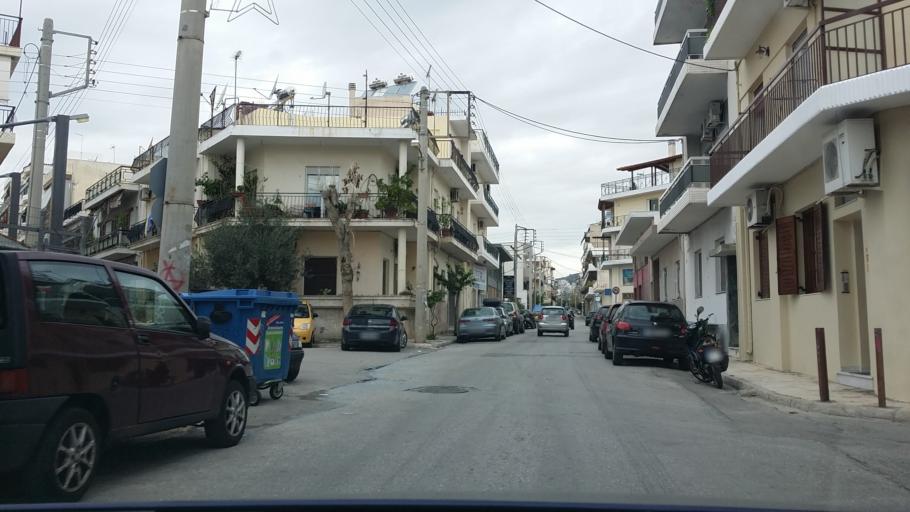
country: GR
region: Attica
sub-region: Nomarchia Athinas
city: Peristeri
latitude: 38.0233
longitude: 23.6937
